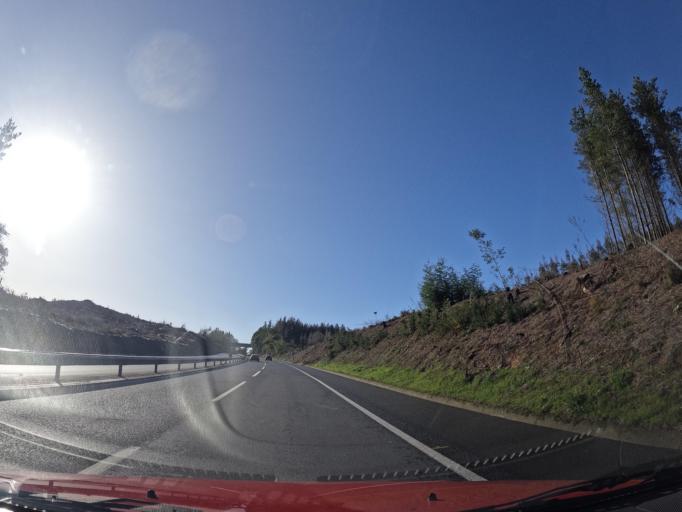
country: CL
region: Biobio
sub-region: Provincia de Concepcion
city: Penco
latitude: -36.7608
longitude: -72.9383
